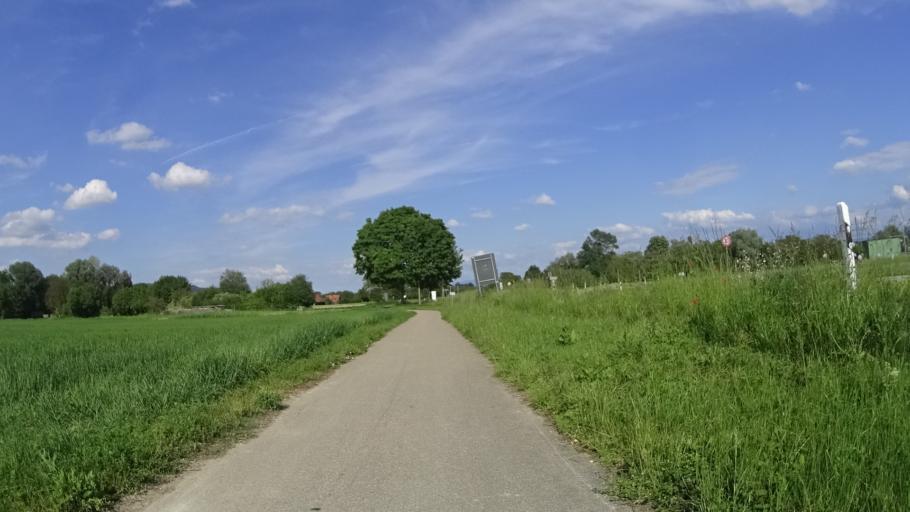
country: DE
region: Baden-Wuerttemberg
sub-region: Freiburg Region
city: Breisach am Rhein
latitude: 48.0293
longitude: 7.5995
